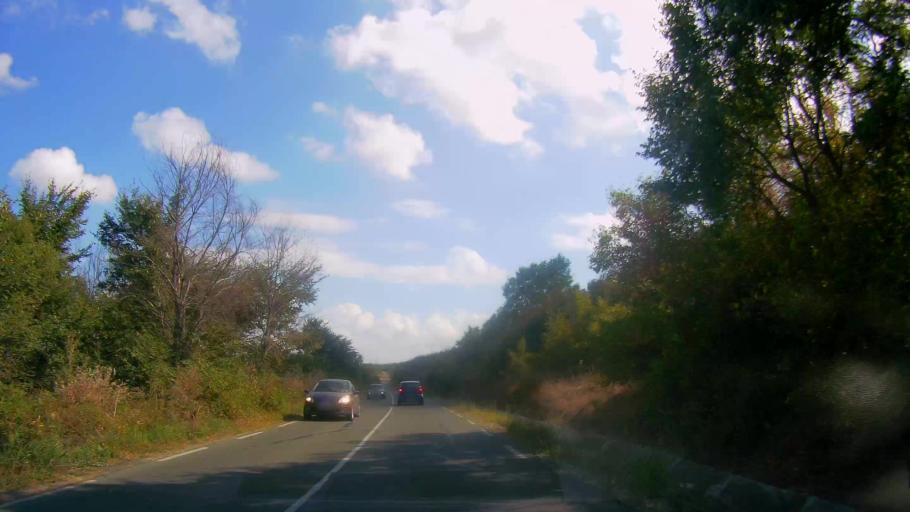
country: BG
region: Burgas
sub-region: Obshtina Kameno
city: Kameno
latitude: 42.4884
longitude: 27.3396
